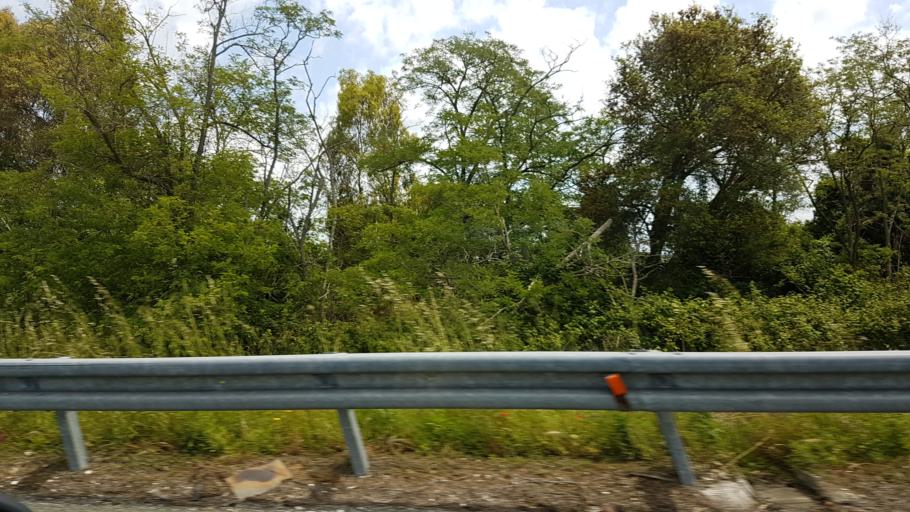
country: IT
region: Tuscany
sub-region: Provincia di Livorno
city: Guasticce
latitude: 43.6169
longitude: 10.3569
